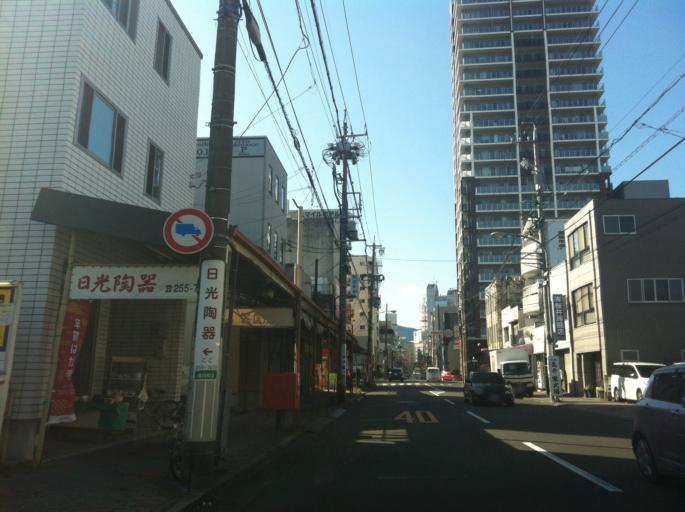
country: JP
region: Shizuoka
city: Shizuoka-shi
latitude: 34.9766
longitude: 138.3935
